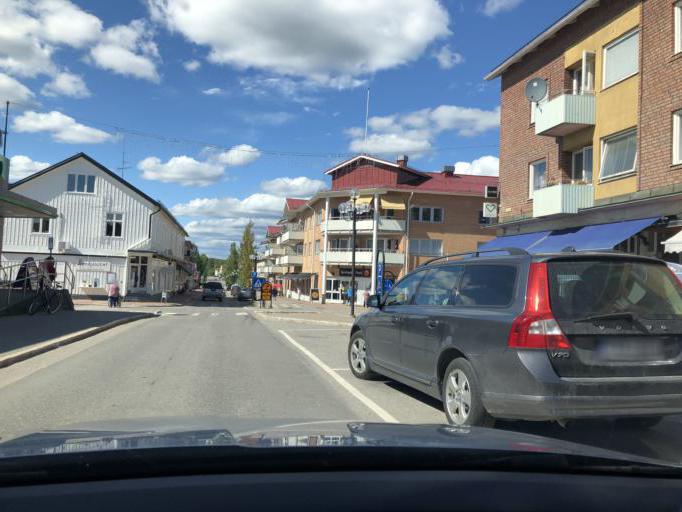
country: SE
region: Norrbotten
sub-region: Alvsbyns Kommun
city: AElvsbyn
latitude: 65.6731
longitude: 21.0104
